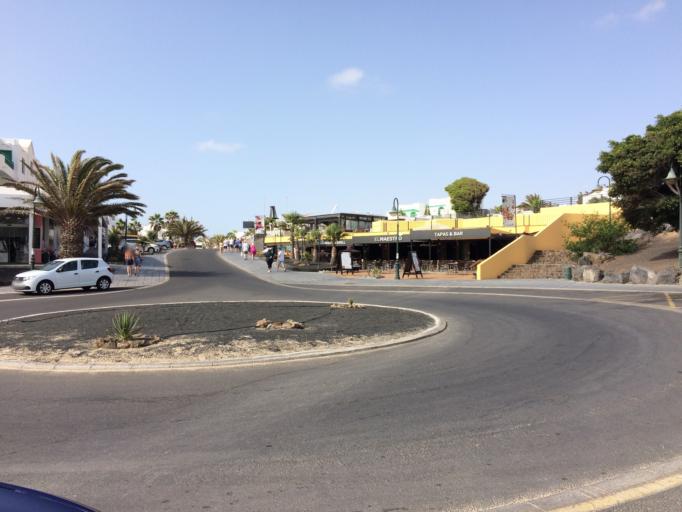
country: ES
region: Canary Islands
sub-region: Provincia de Las Palmas
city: Arrecife
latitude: 28.9976
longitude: -13.4897
